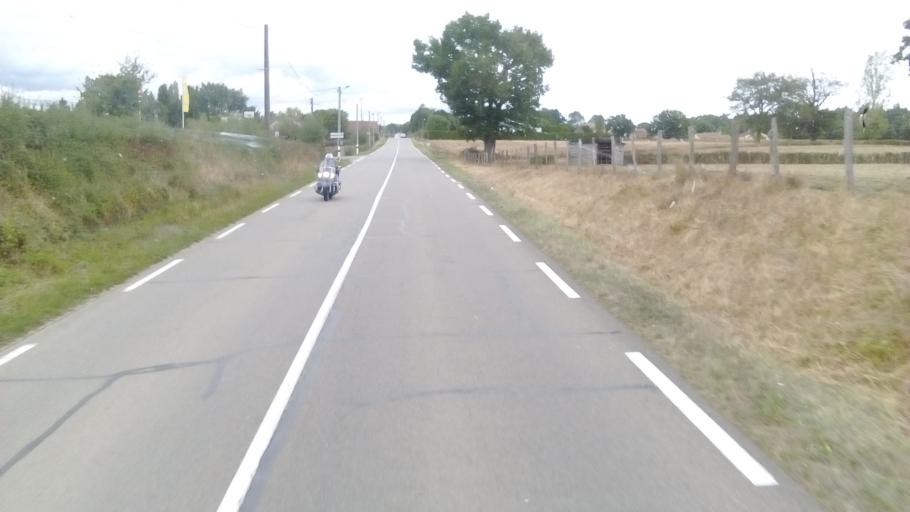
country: FR
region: Bourgogne
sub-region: Departement de Saone-et-Loire
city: Saint-Yan
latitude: 46.4466
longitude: 4.0172
